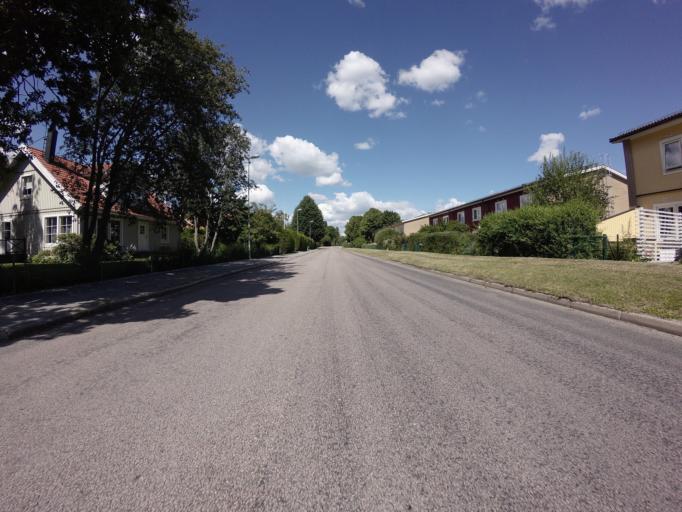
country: SE
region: Stockholm
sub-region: Sollentuna Kommun
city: Sollentuna
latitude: 59.4608
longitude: 17.9199
